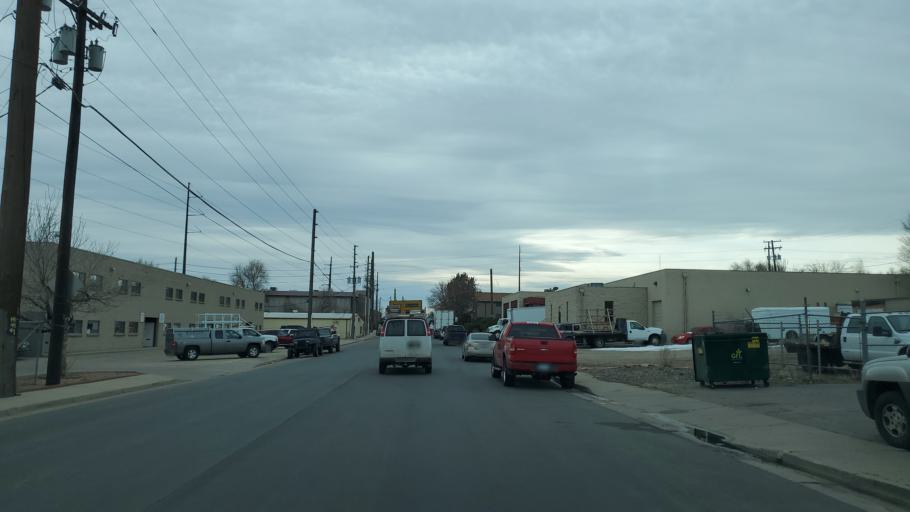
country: US
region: Colorado
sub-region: Denver County
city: Denver
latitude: 39.6962
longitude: -105.0016
